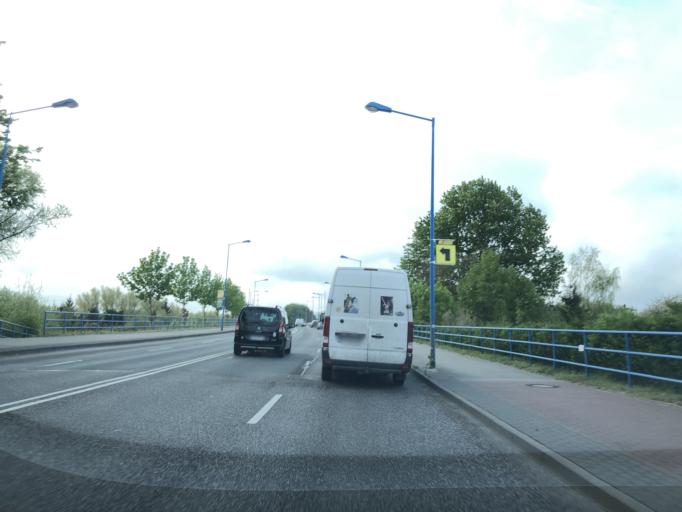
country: DE
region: Mecklenburg-Vorpommern
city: Guestrow
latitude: 53.7986
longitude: 12.1818
